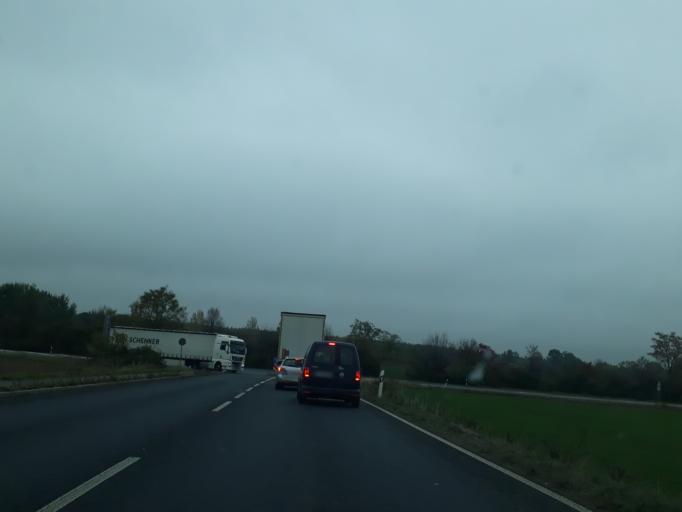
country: DE
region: Saxony
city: Radeburg
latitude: 51.2108
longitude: 13.7421
